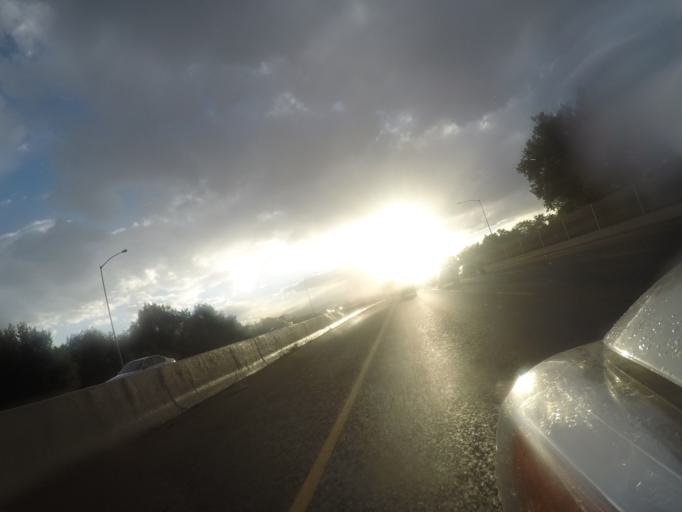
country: US
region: Colorado
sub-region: Arapahoe County
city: Sheridan
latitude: 39.6544
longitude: -105.0399
